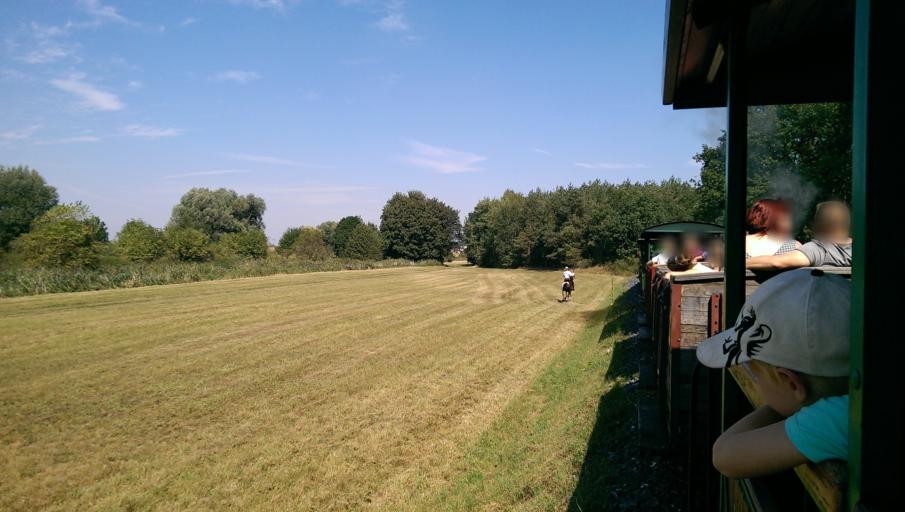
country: CZ
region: Central Bohemia
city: Stary Kolin
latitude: 50.0584
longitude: 15.2672
